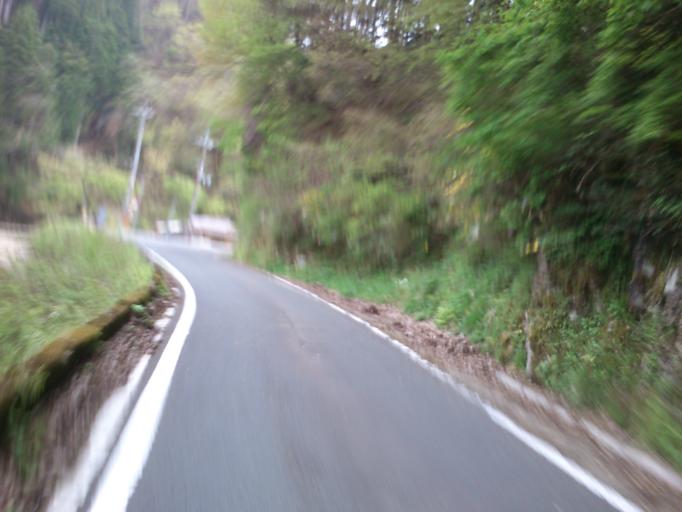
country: JP
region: Kyoto
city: Maizuru
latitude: 35.3878
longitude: 135.4732
